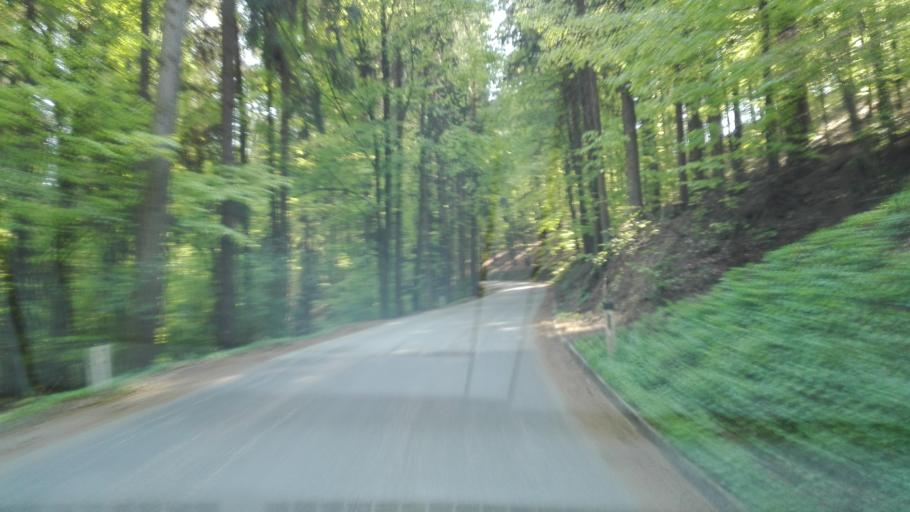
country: AT
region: Upper Austria
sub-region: Politischer Bezirk Rohrbach
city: Atzesberg
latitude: 48.4242
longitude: 13.9178
